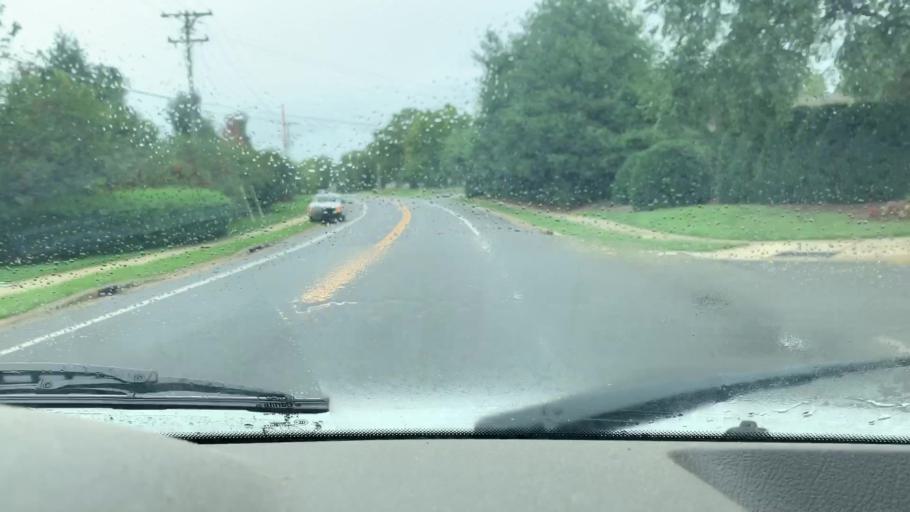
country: US
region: North Carolina
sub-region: Mecklenburg County
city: Cornelius
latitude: 35.4842
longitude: -80.8945
